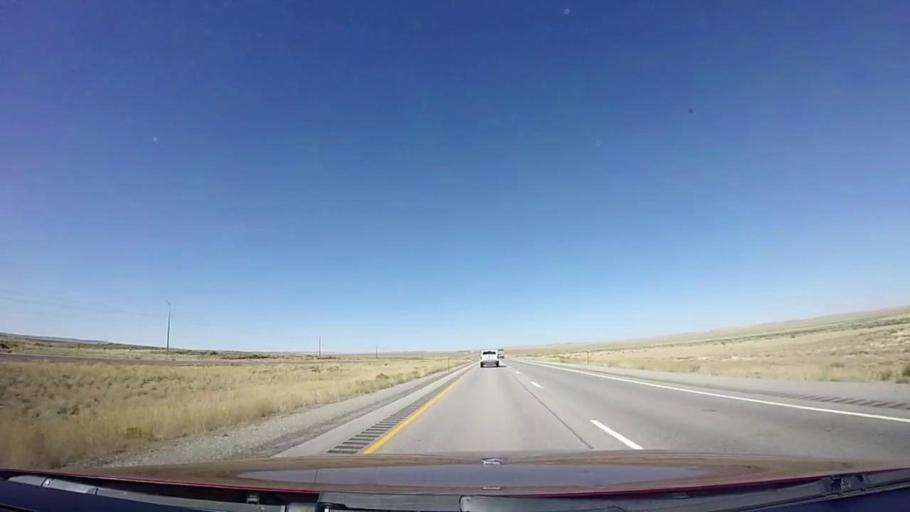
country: US
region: Wyoming
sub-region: Carbon County
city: Rawlins
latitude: 41.7797
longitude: -107.4361
